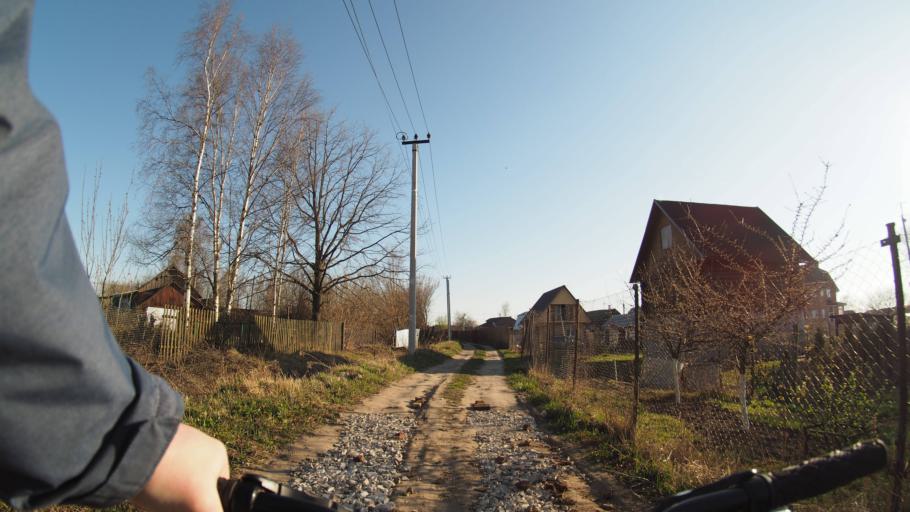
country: RU
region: Moskovskaya
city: Malyshevo
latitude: 55.5003
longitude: 38.3500
